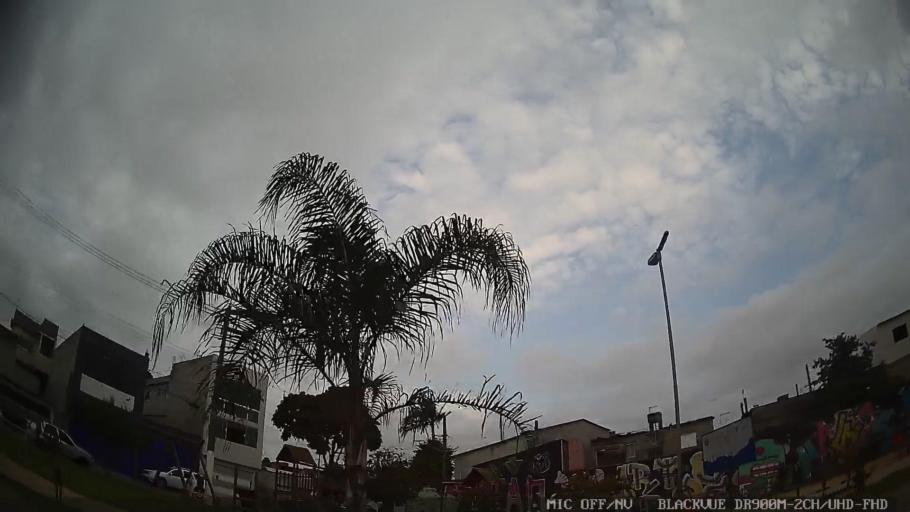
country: BR
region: Sao Paulo
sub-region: Itaquaquecetuba
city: Itaquaquecetuba
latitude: -23.4918
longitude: -46.3951
